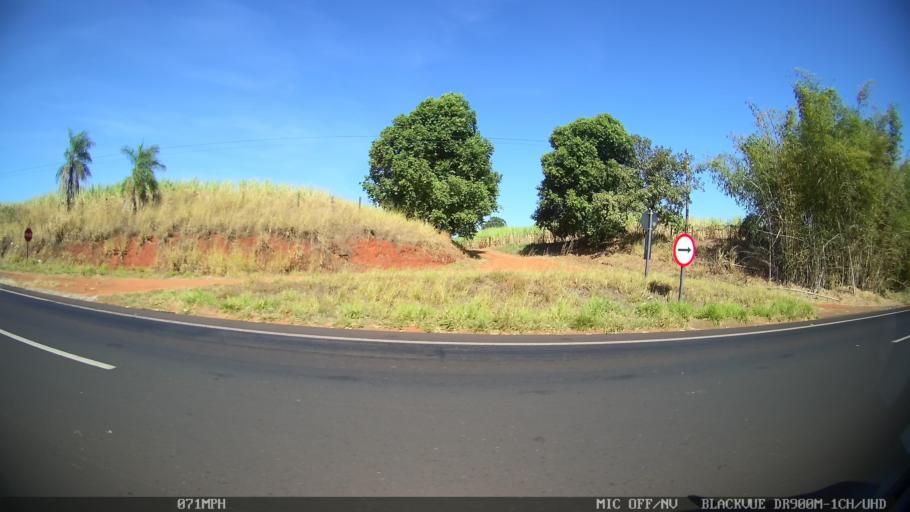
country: BR
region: Sao Paulo
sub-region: Barretos
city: Barretos
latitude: -20.6003
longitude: -48.7260
